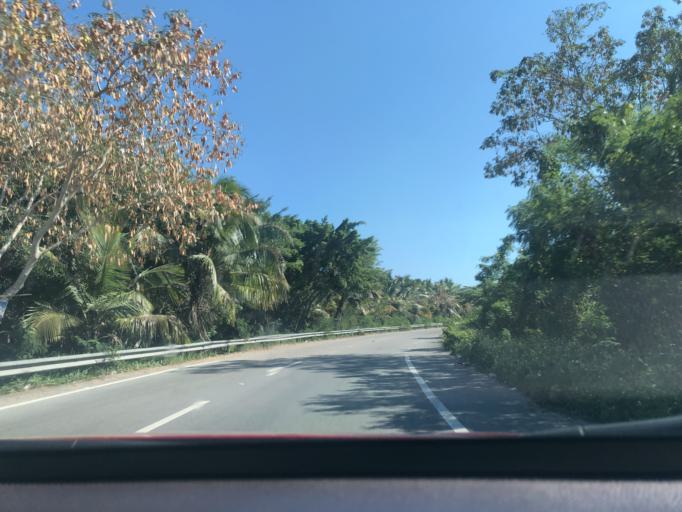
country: DO
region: Santo Domingo
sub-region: Santo Domingo
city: Boca Chica
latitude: 18.4515
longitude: -69.5973
